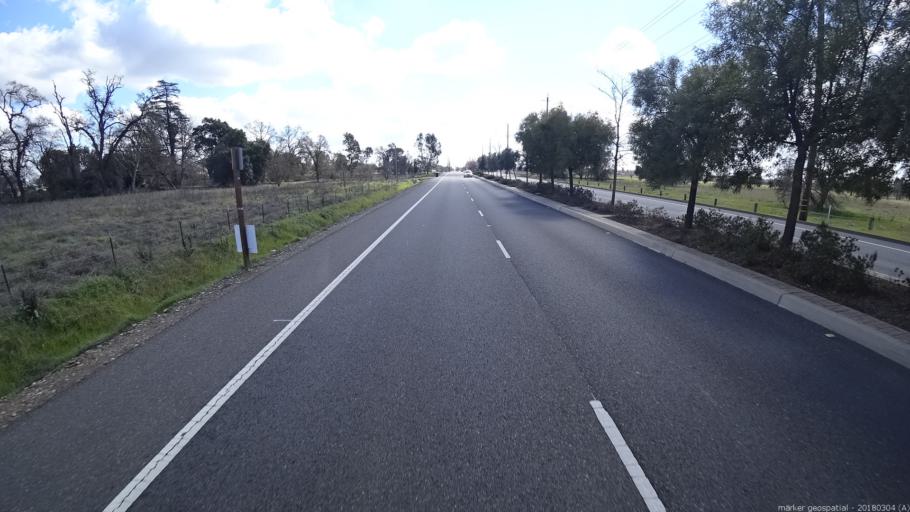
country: US
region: California
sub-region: Sacramento County
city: Vineyard
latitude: 38.4607
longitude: -121.3347
